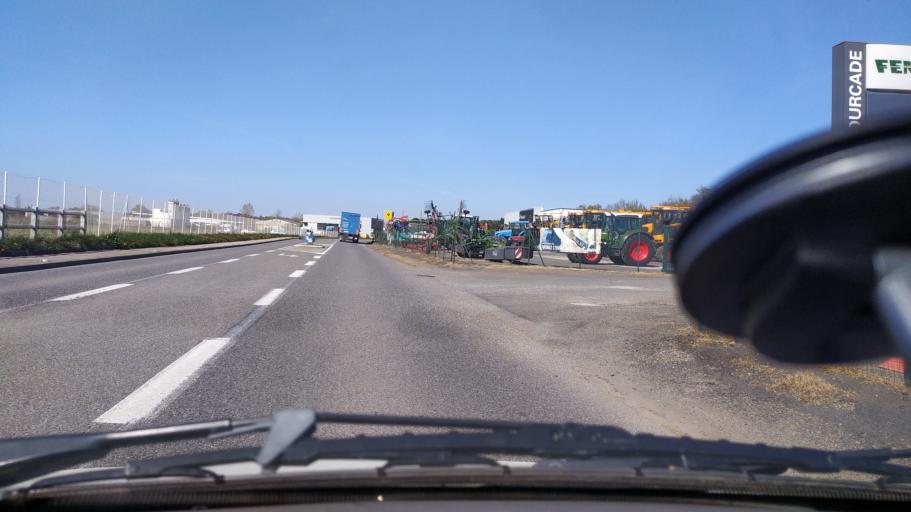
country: FR
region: Midi-Pyrenees
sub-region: Departement du Gers
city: Nogaro
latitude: 43.7661
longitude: -0.0317
